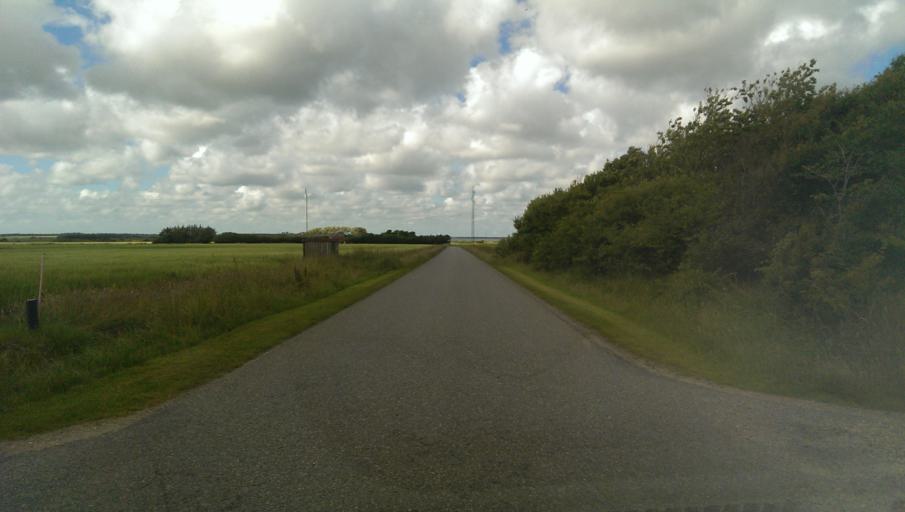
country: DK
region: Central Jutland
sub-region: Holstebro Kommune
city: Ulfborg
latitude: 56.2753
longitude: 8.2479
